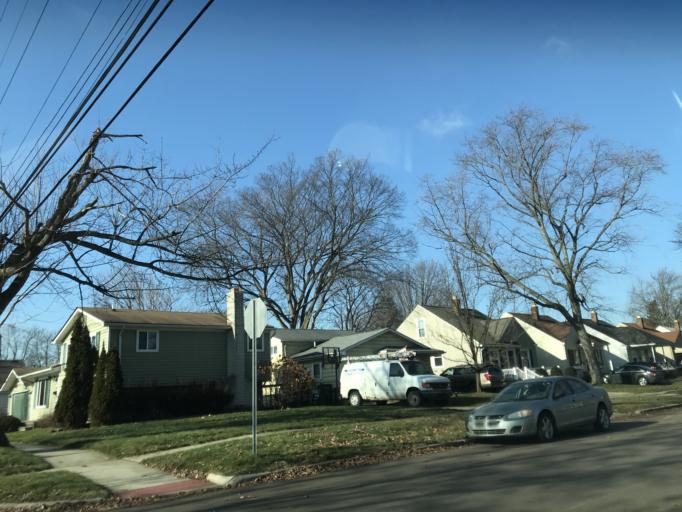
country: US
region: Michigan
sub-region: Oakland County
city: Madison Heights
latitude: 42.4965
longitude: -83.1199
